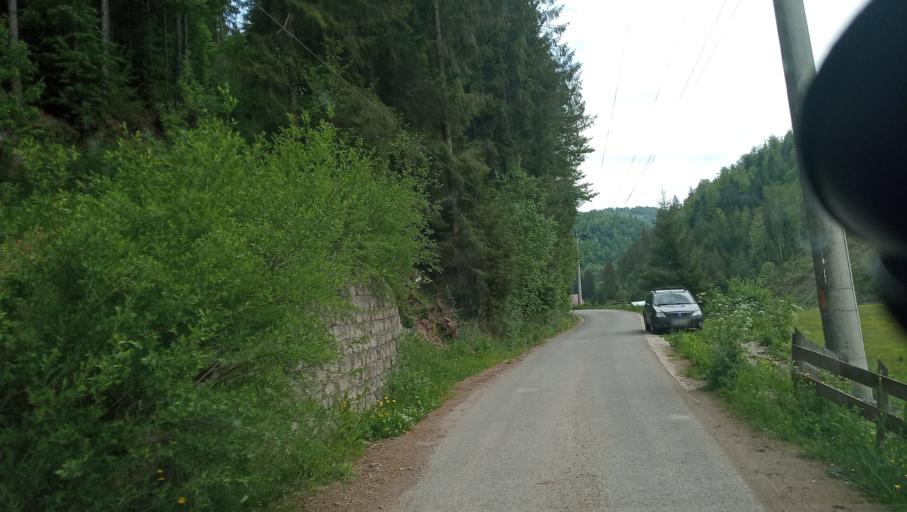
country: RO
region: Alba
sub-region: Comuna Garda de Sus
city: Garda de Sus
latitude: 46.4788
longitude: 22.8002
